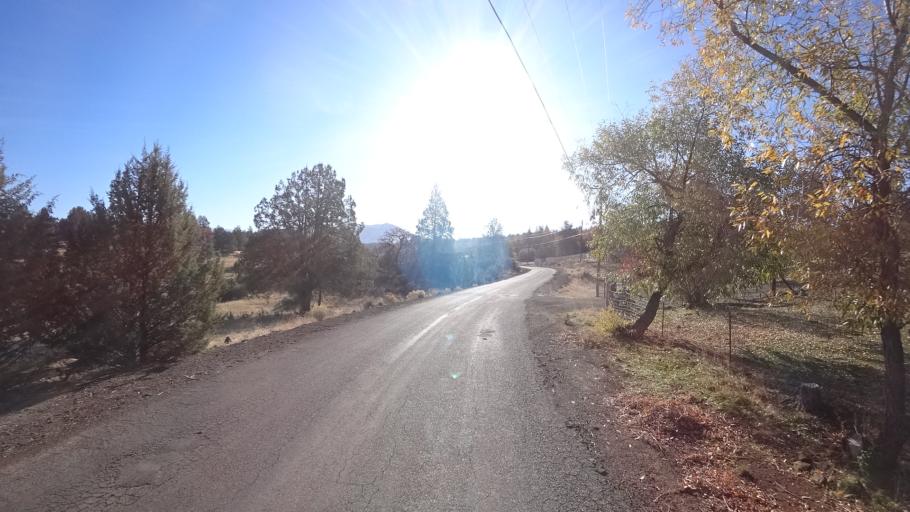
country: US
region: California
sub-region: Siskiyou County
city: Montague
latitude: 41.8818
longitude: -122.4531
